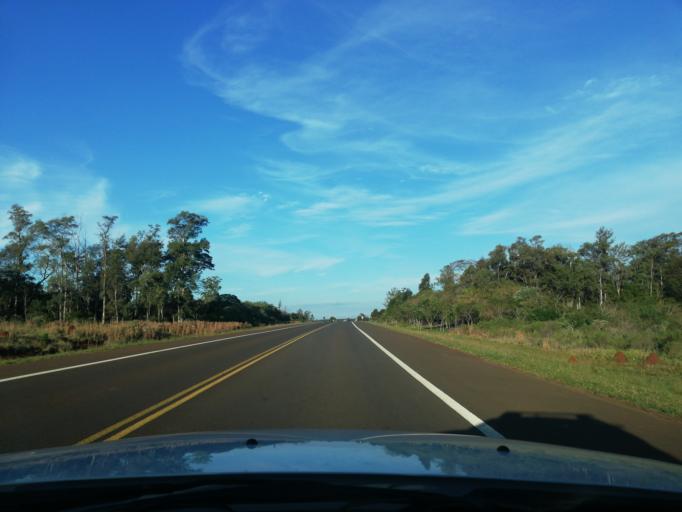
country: AR
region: Misiones
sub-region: Departamento de Capital
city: Posadas
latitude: -27.4617
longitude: -55.9859
